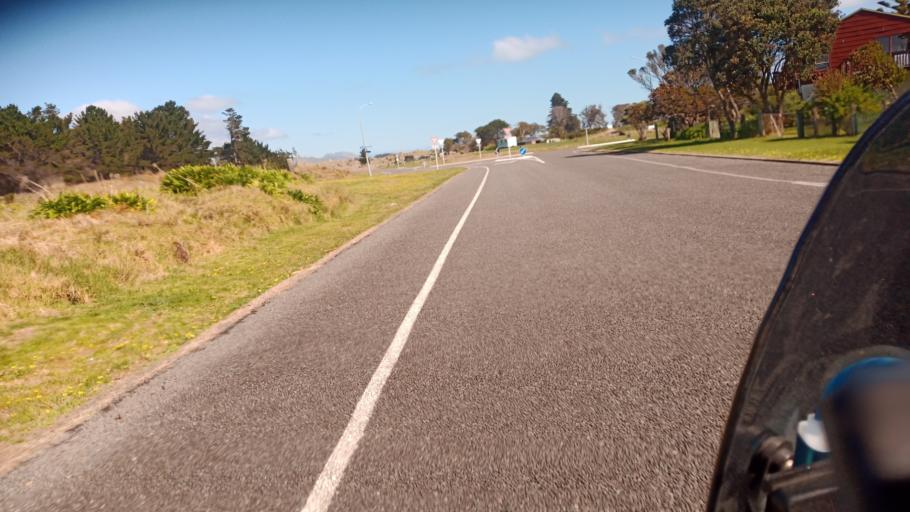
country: NZ
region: Gisborne
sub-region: Gisborne District
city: Gisborne
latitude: -39.0173
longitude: 177.8848
